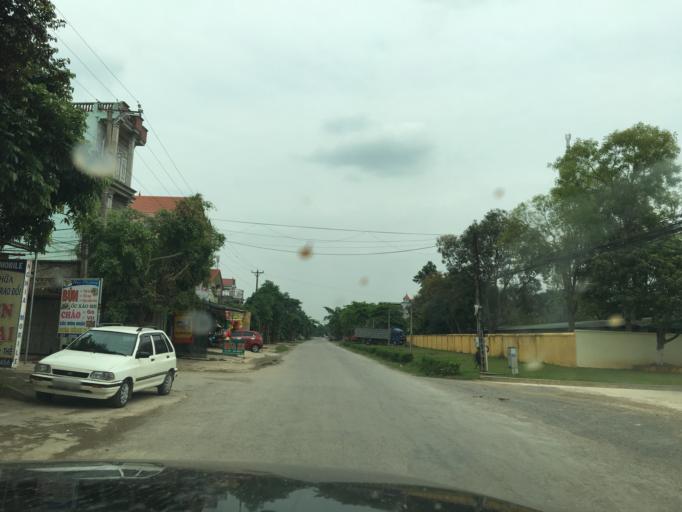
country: VN
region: Ninh Binh
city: Thi Tran Nho Quan
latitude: 20.2373
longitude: 105.8054
